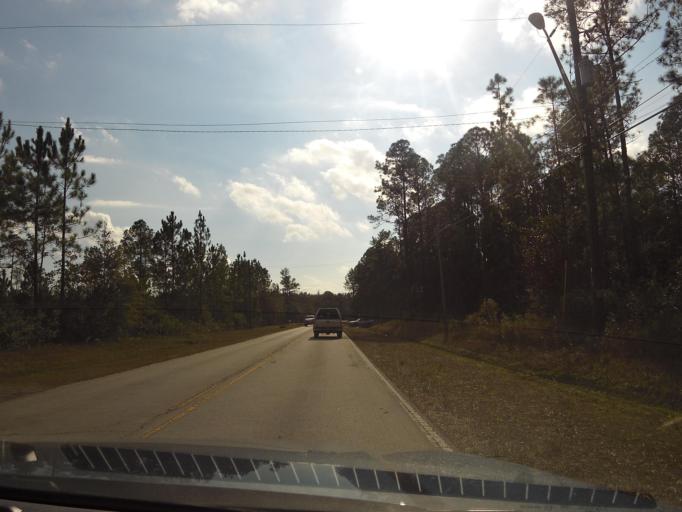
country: US
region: Florida
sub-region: Duval County
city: Baldwin
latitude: 30.1886
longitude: -81.9911
